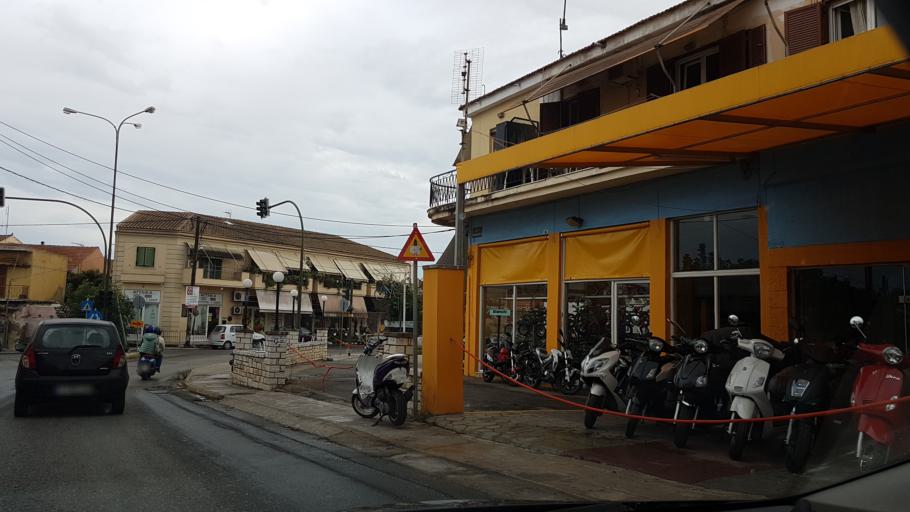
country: GR
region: Ionian Islands
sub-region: Nomos Kerkyras
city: Kerkyra
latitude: 39.6192
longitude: 19.9080
